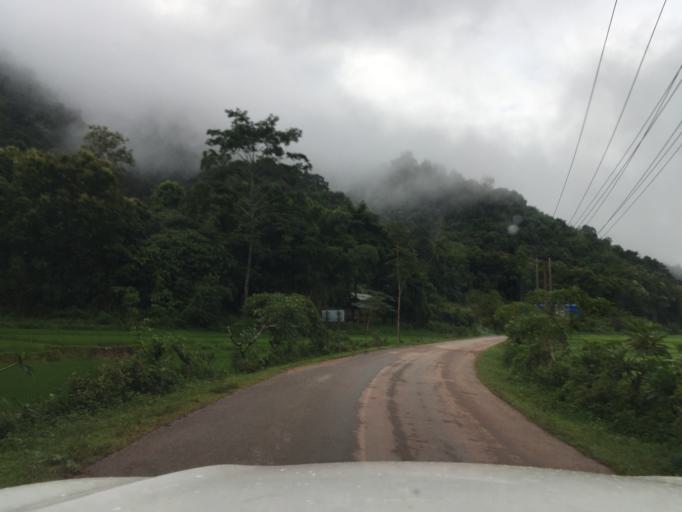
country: LA
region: Oudomxai
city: Muang La
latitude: 20.8390
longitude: 102.1029
